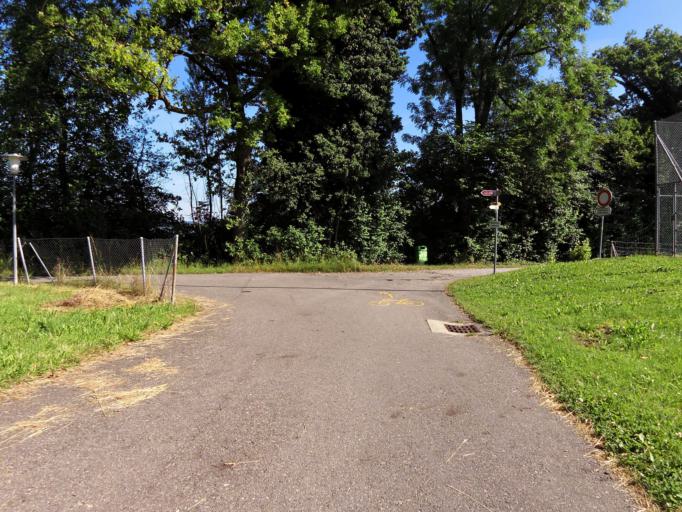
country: CH
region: Thurgau
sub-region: Kreuzlingen District
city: Munsterlingen
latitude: 47.6323
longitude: 9.2392
